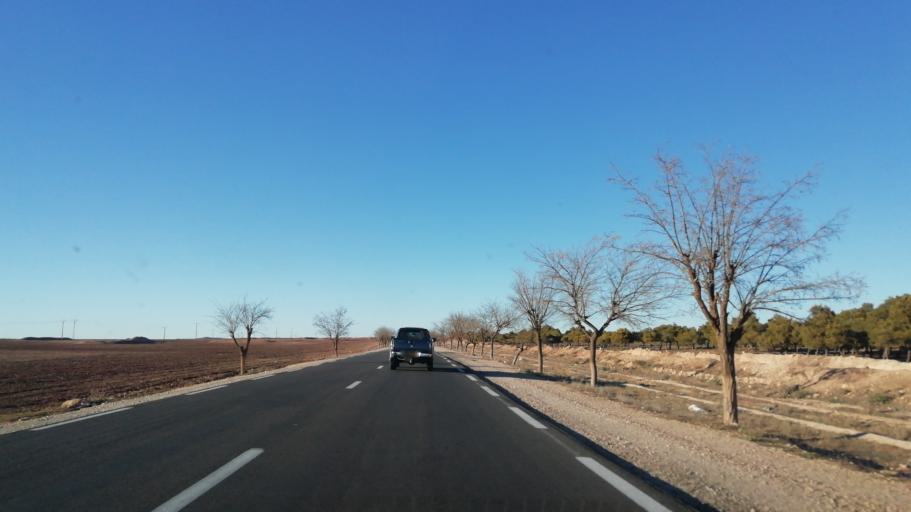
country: DZ
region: Tlemcen
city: Sebdou
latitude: 34.5343
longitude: -1.2974
